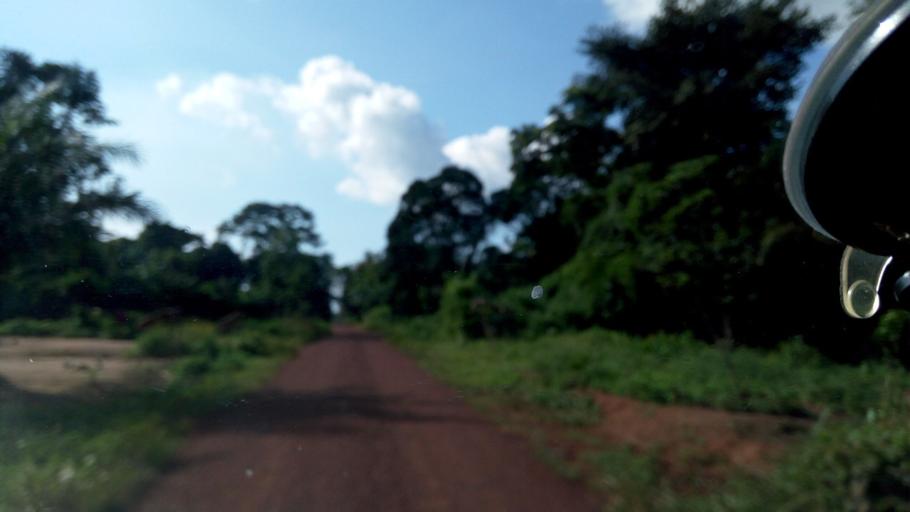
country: CD
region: Equateur
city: Libenge
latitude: 3.8107
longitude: 18.7030
